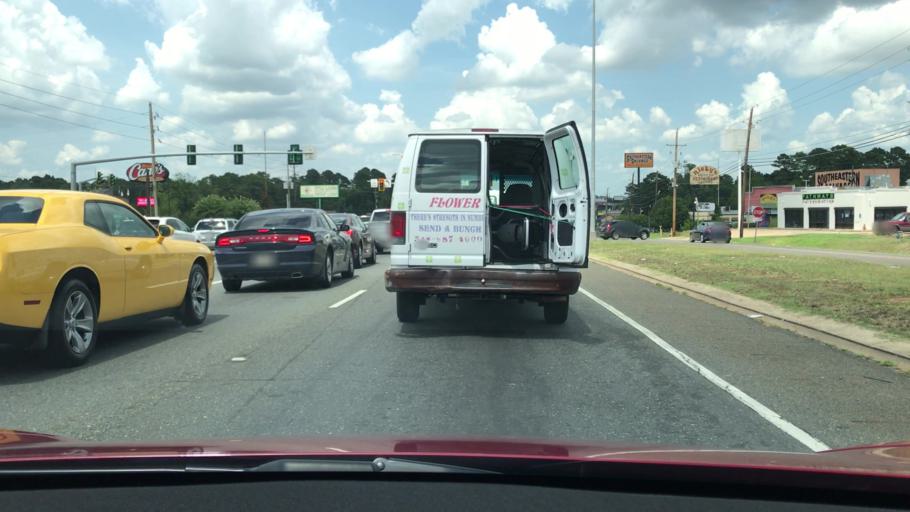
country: US
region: Louisiana
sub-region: Bossier Parish
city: Bossier City
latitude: 32.4102
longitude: -93.7963
